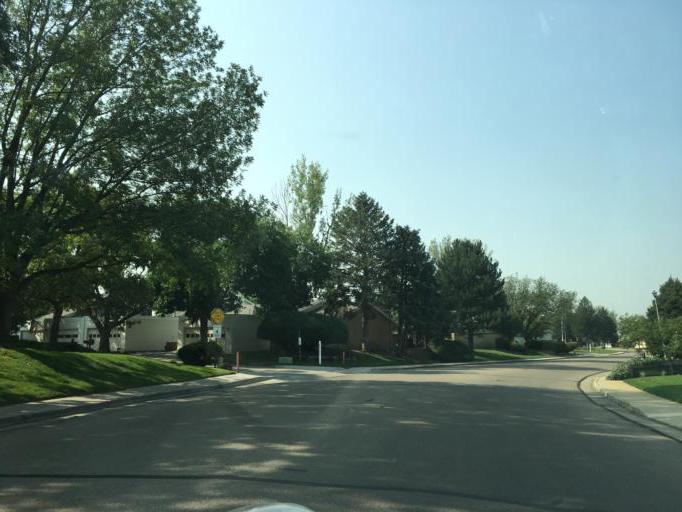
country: US
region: Colorado
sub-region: Adams County
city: Brighton
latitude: 39.9833
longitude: -104.7941
